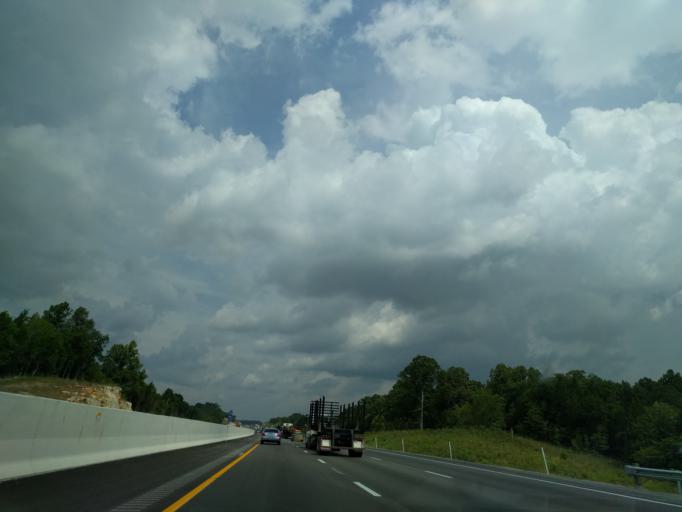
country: US
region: Kentucky
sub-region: Hart County
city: Munfordville
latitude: 37.4100
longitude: -85.8814
